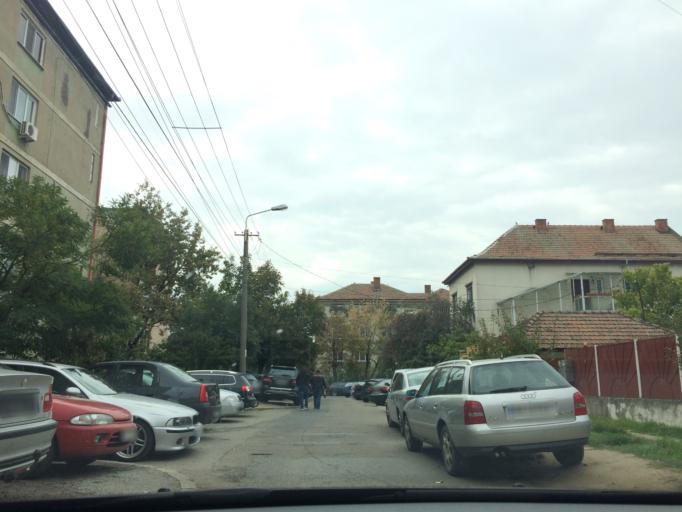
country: RO
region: Timis
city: Timisoara
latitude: 45.7456
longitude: 21.2373
